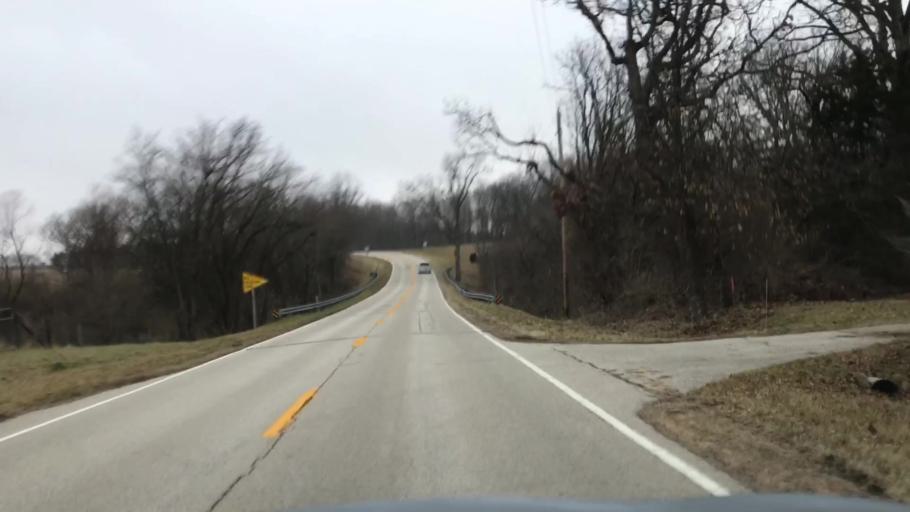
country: US
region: Illinois
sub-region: McLean County
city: Hudson
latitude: 40.6269
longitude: -88.9244
